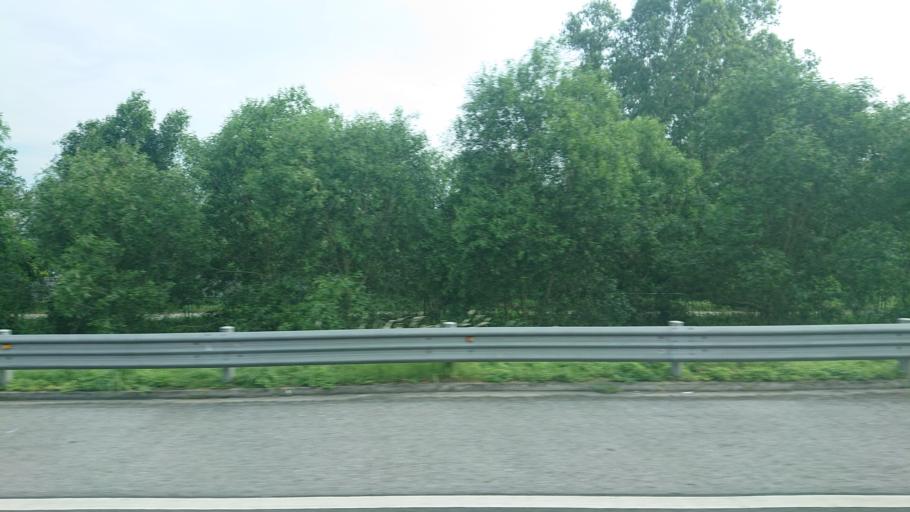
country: VN
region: Hai Phong
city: An Lao
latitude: 20.7896
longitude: 106.5544
